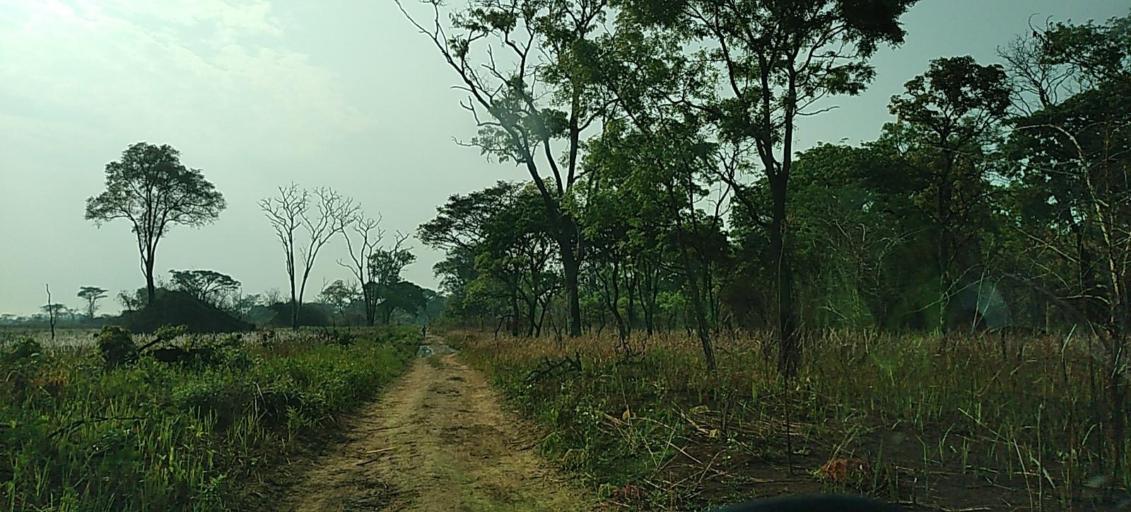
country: ZM
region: North-Western
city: Solwezi
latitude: -12.3883
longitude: 26.5708
